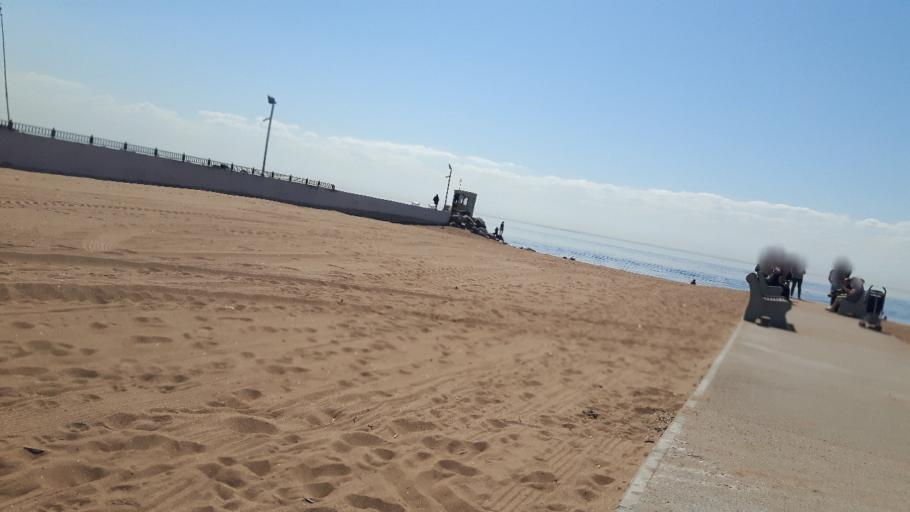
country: RU
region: St.-Petersburg
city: Zelenogorsk
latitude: 60.1875
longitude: 29.6996
